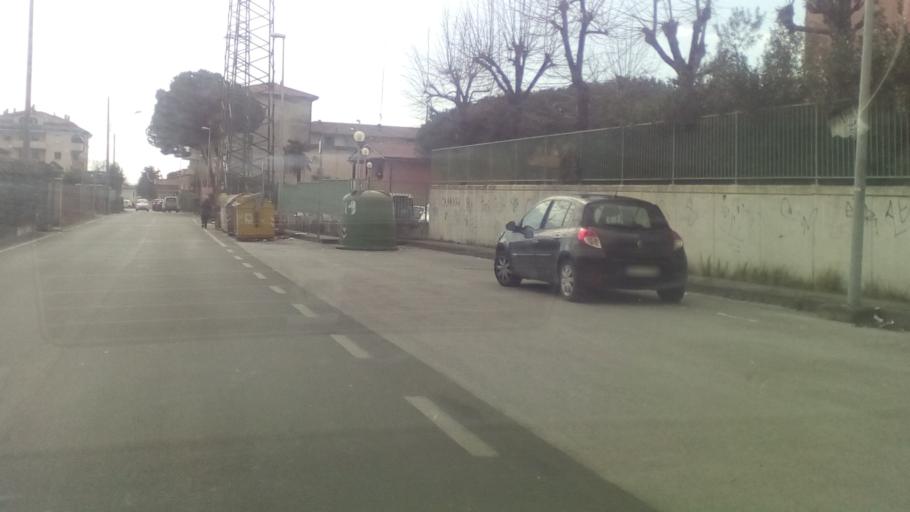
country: IT
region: Tuscany
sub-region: Provincia di Massa-Carrara
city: Carrara
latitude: 44.0595
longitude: 10.0725
